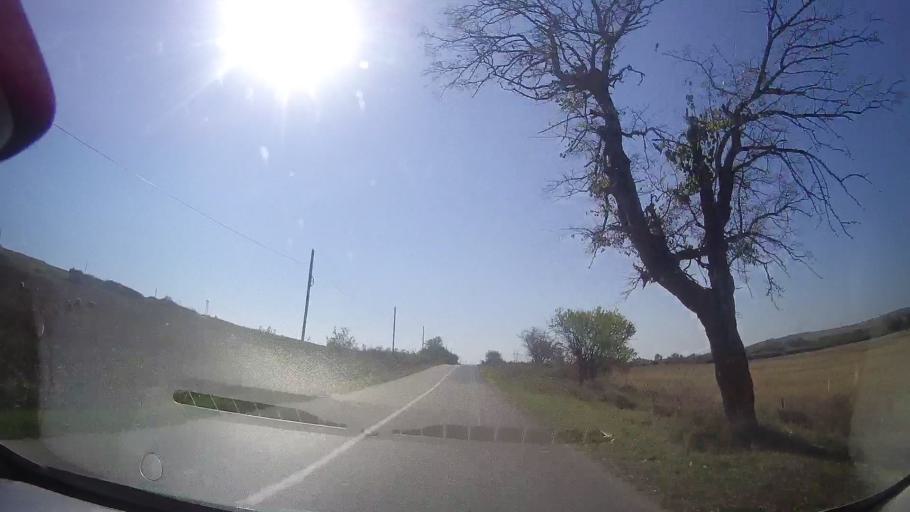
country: RO
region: Timis
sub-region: Comuna Bethausen
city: Bethausen
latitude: 45.8493
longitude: 21.9636
